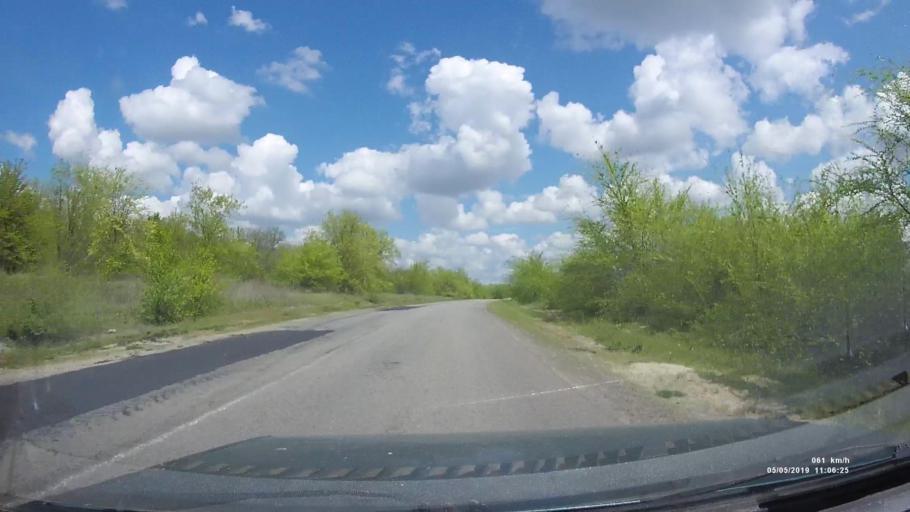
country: RU
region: Rostov
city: Ust'-Donetskiy
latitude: 47.7152
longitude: 40.9109
